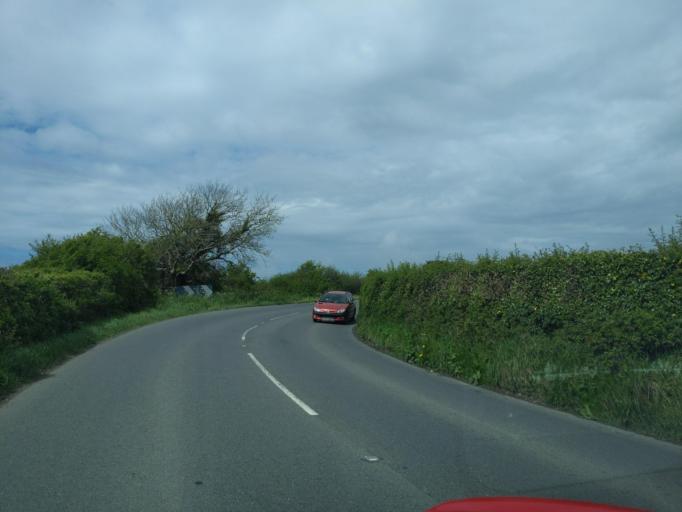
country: GB
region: England
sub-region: Cornwall
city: Wadebridge
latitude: 50.5479
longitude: -4.8645
